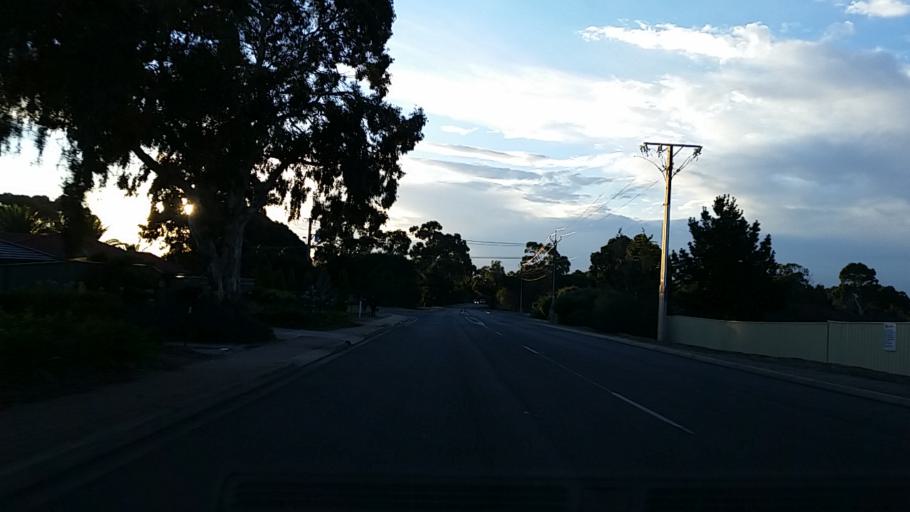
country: AU
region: South Australia
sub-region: Onkaparinga
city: Craigburn Farm
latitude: -35.0623
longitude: 138.6065
